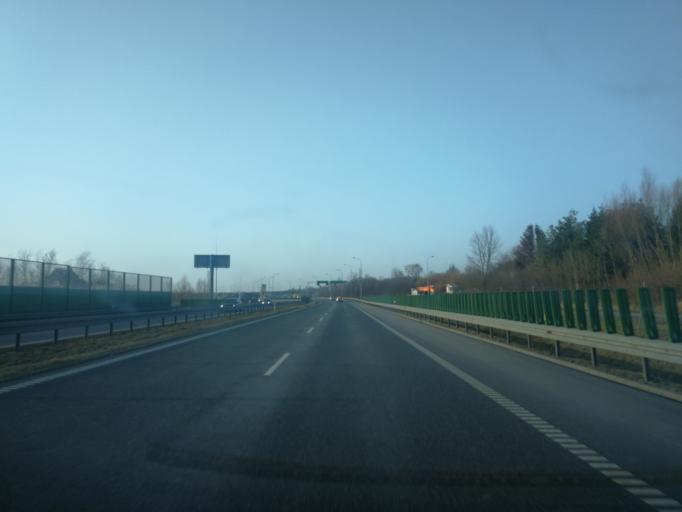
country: PL
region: Warmian-Masurian Voivodeship
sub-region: Powiat elblaski
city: Gronowo Gorne
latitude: 54.1340
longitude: 19.4556
